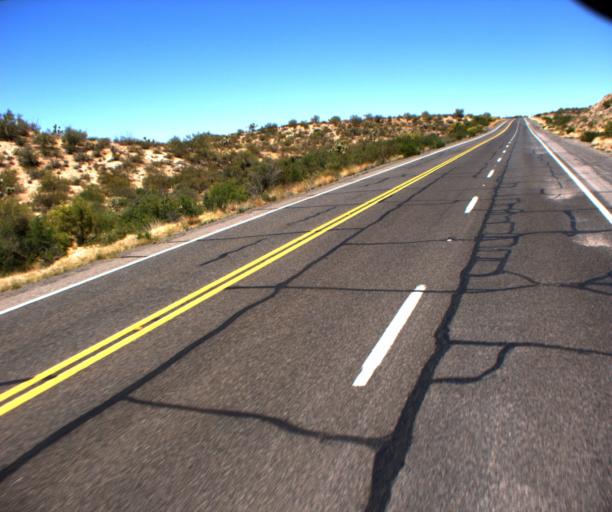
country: US
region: Arizona
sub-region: Yavapai County
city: Congress
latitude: 34.2157
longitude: -113.0671
